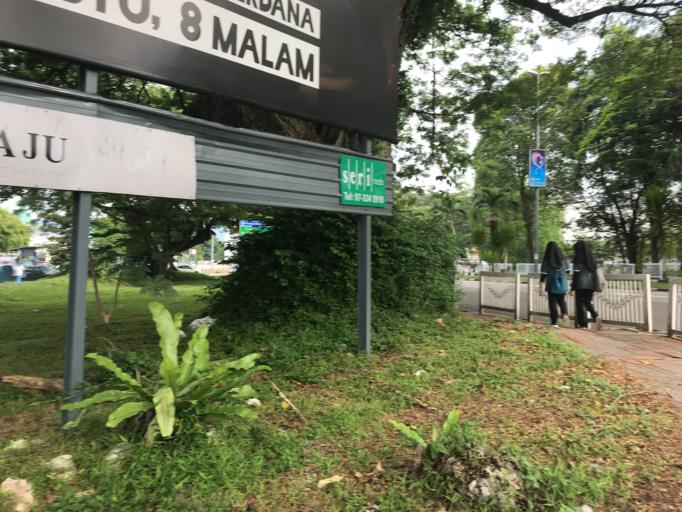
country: MY
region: Perak
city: Ipoh
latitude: 4.6038
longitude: 101.0937
